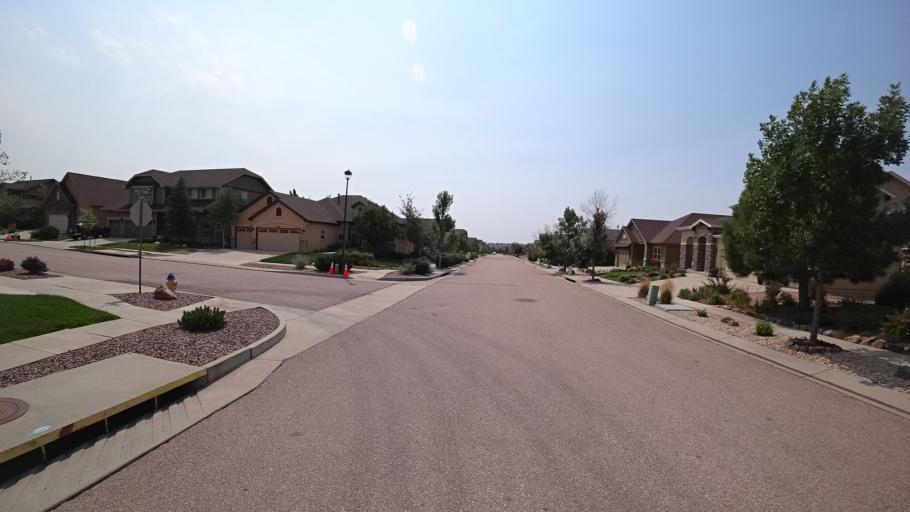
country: US
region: Colorado
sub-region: El Paso County
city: Black Forest
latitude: 38.9648
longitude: -104.7221
